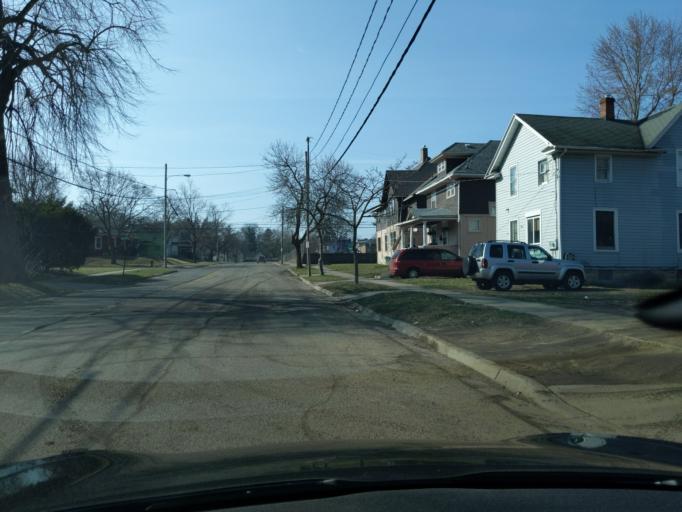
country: US
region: Michigan
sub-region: Jackson County
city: Jackson
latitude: 42.2419
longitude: -84.4118
